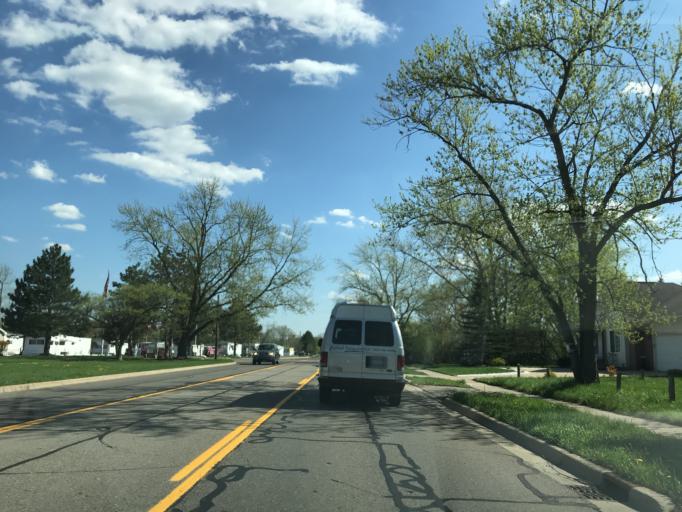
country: US
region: Michigan
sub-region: Oakland County
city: Farmington
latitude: 42.4595
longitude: -83.3372
